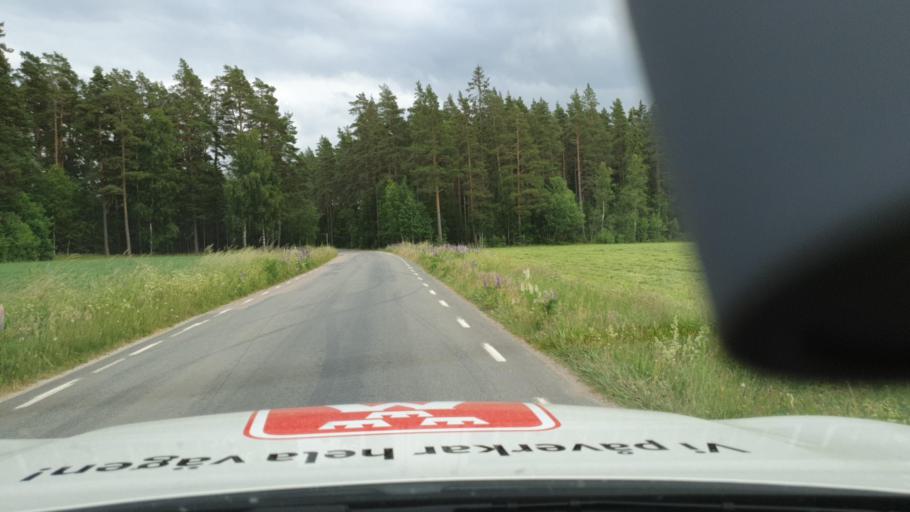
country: SE
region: Vaestra Goetaland
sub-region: Tidaholms Kommun
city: Olofstorp
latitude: 58.1920
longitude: 14.0356
